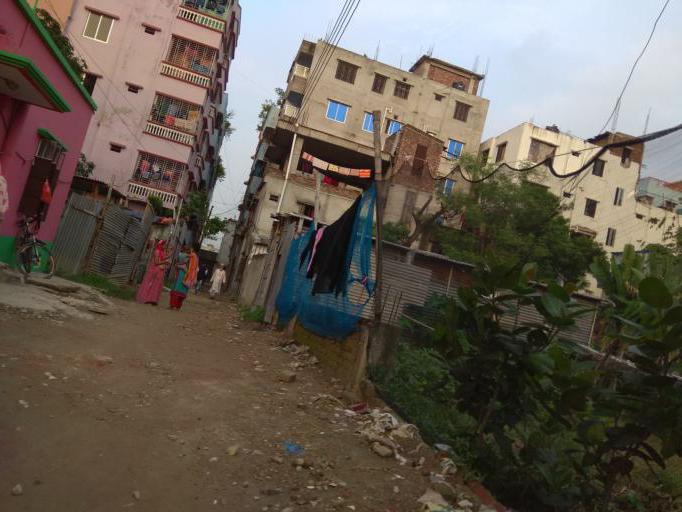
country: BD
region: Dhaka
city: Tungi
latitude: 23.8145
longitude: 90.3799
